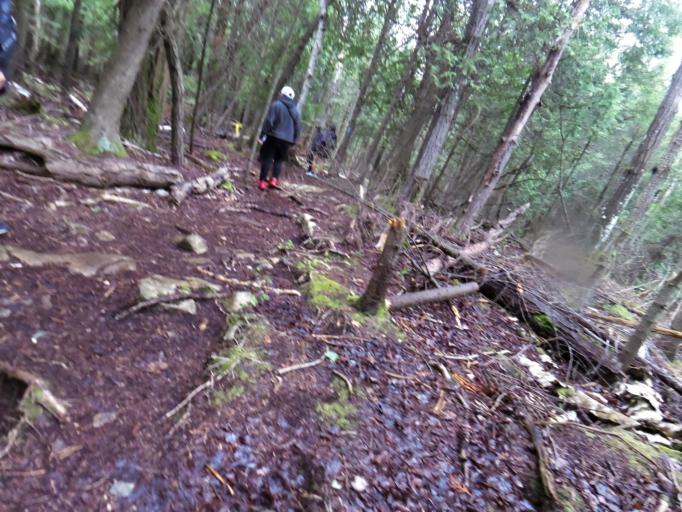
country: CA
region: Ontario
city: Tobermory
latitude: 45.2611
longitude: -81.6424
